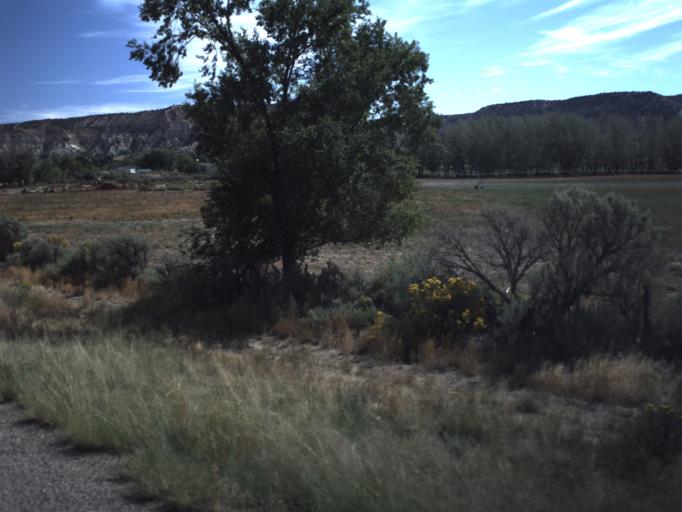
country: US
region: Utah
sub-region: Garfield County
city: Panguitch
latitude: 37.5614
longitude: -112.0144
